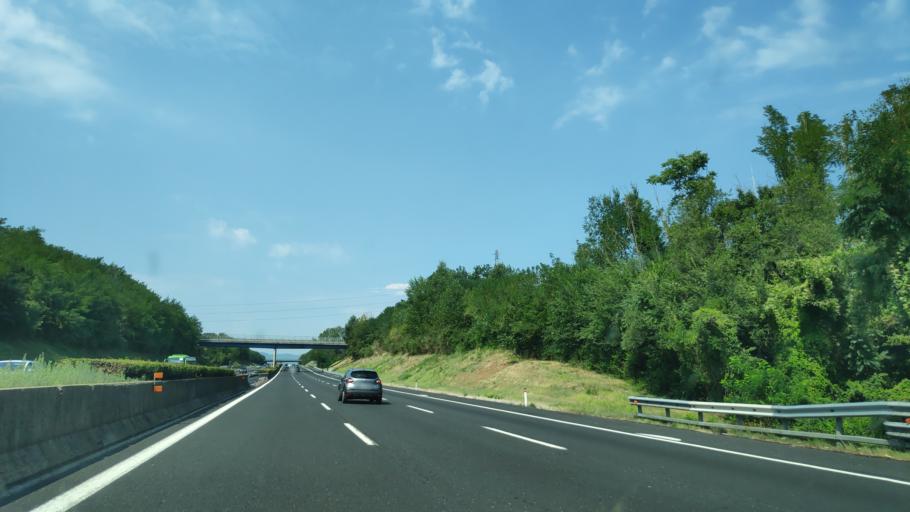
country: IT
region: Latium
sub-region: Provincia di Frosinone
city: Ceprano
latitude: 41.5438
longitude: 13.5427
